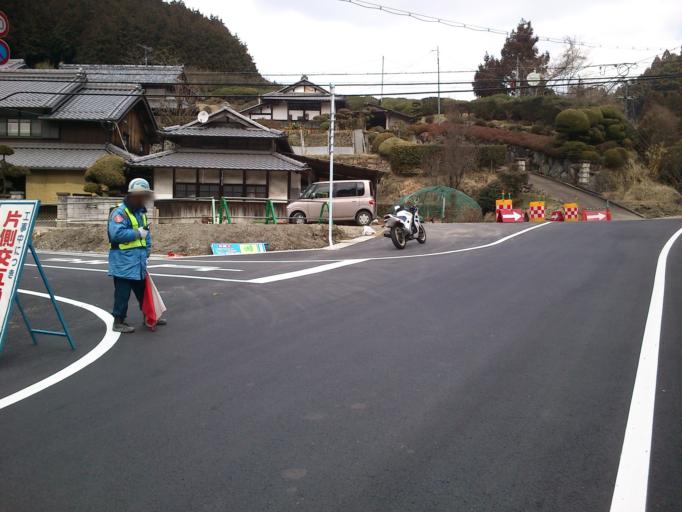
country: JP
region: Kyoto
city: Uji
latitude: 34.8302
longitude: 135.9482
